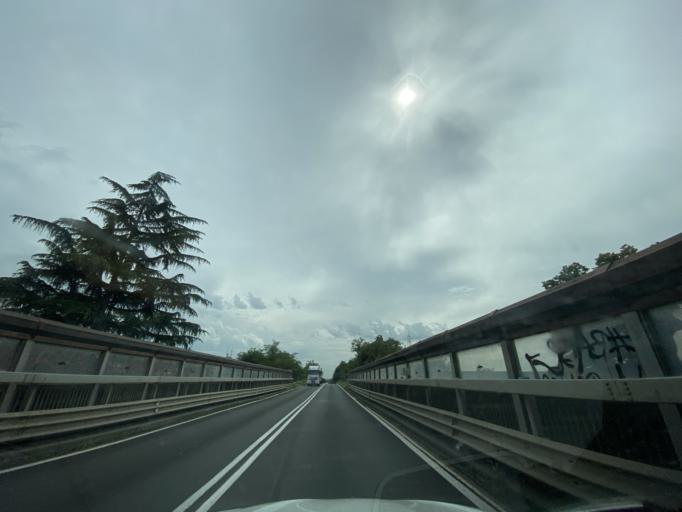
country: IT
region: Lombardy
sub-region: Citta metropolitana di Milano
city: Gorgonzola
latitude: 45.5276
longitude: 9.3967
